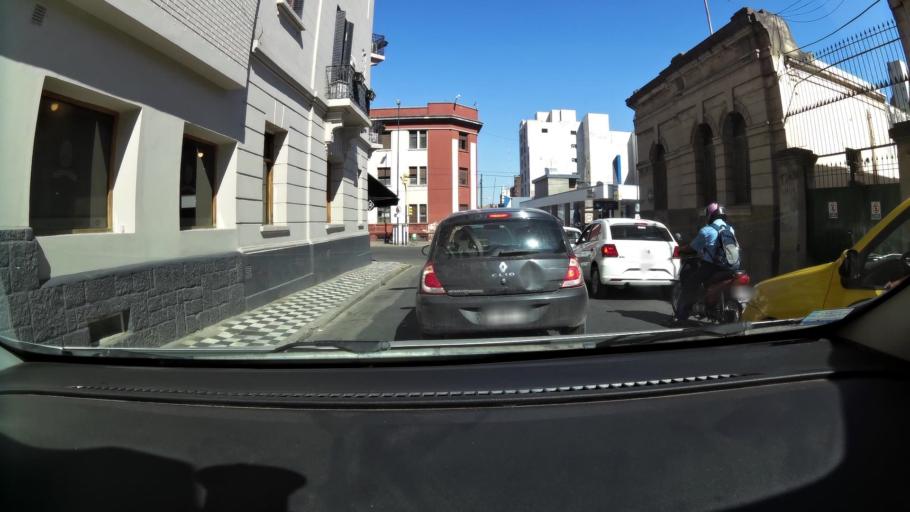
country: AR
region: Cordoba
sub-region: Departamento de Capital
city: Cordoba
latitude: -31.4225
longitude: -64.1895
